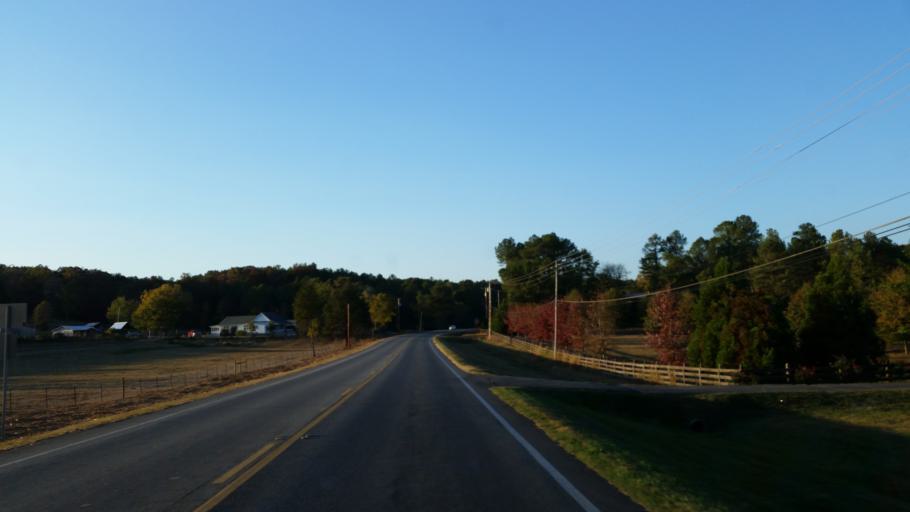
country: US
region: Georgia
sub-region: Gordon County
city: Calhoun
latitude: 34.5249
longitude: -84.9709
